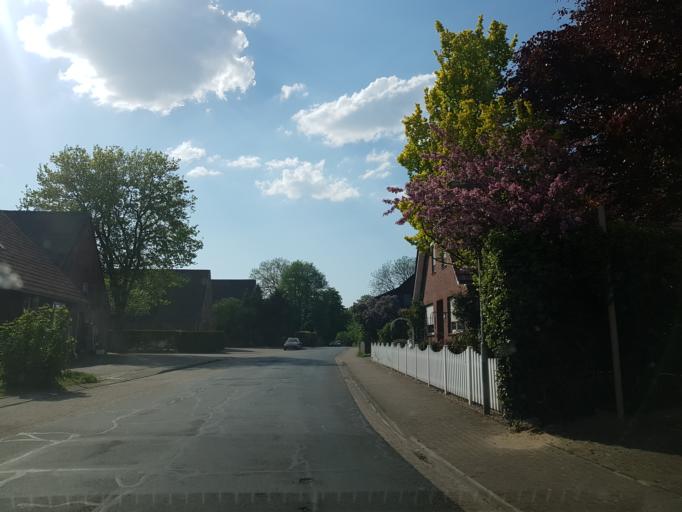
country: DE
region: Lower Saxony
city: Langen
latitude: 53.6461
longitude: 8.6017
